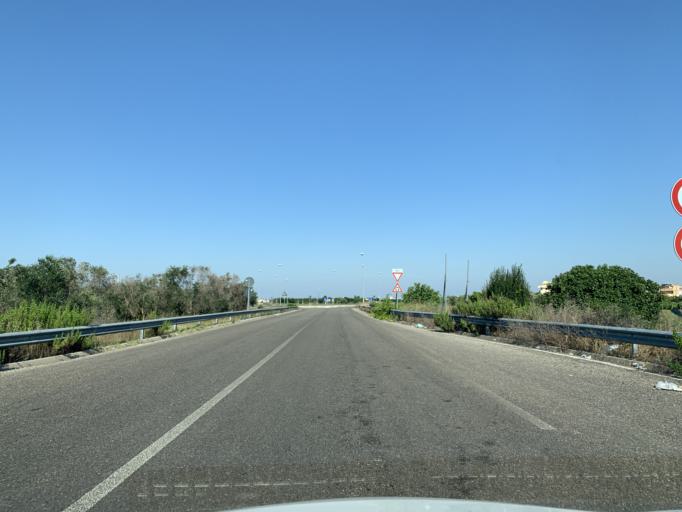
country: IT
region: Apulia
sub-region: Provincia di Lecce
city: Nardo
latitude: 40.1885
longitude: 18.0303
